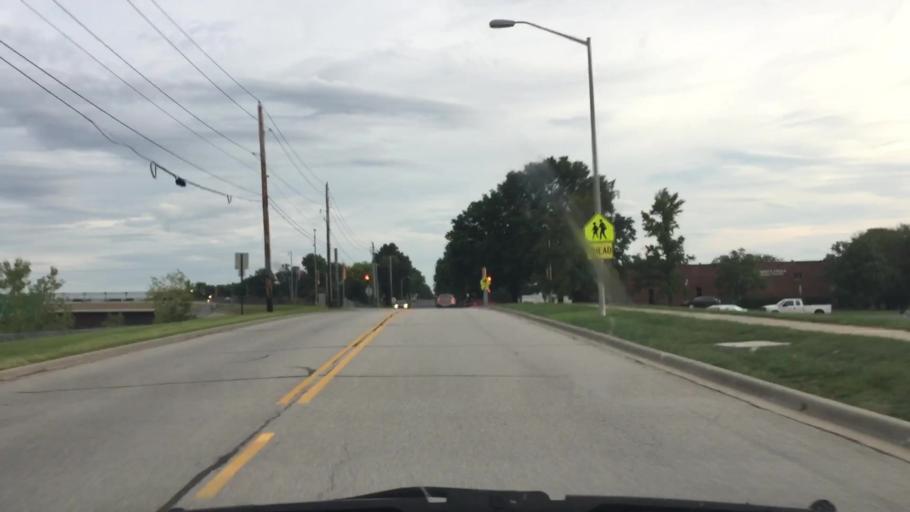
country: US
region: Kansas
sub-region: Johnson County
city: Lenexa
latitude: 38.9647
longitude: -94.7143
